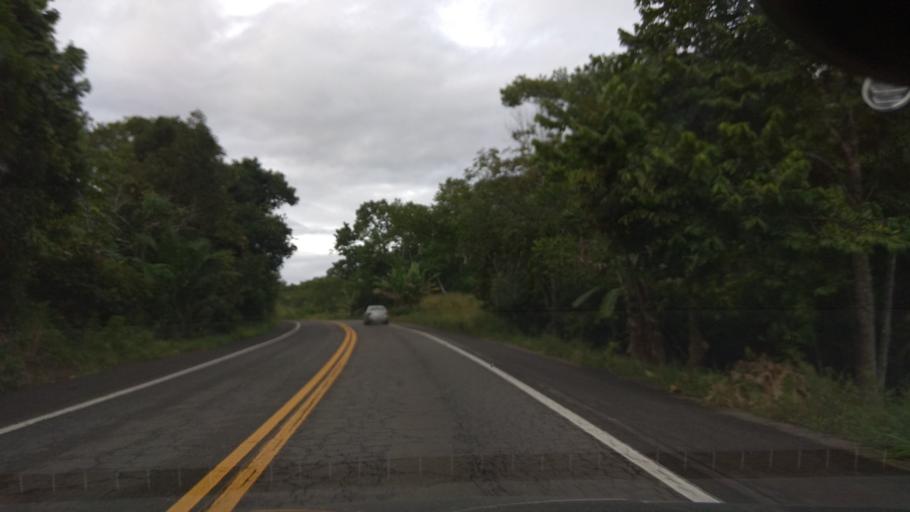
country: BR
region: Bahia
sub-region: Ubaitaba
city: Ubaitaba
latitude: -14.2627
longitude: -39.3386
